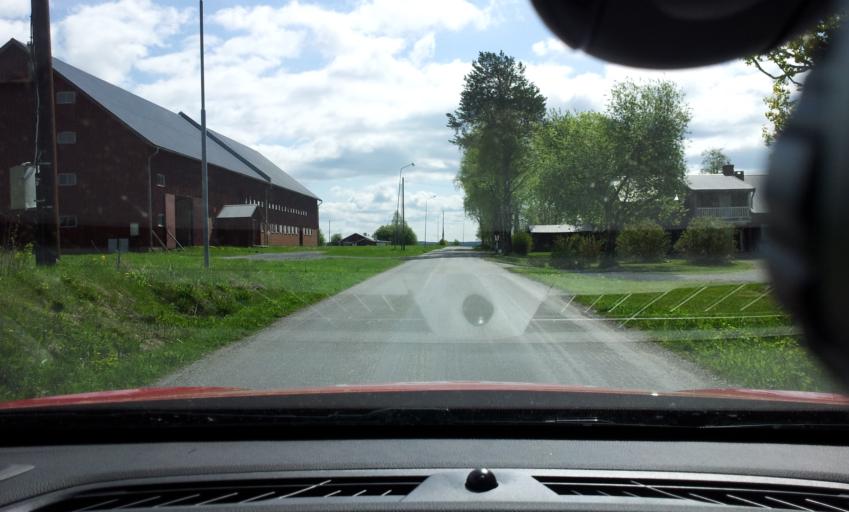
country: SE
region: Jaemtland
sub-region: OEstersunds Kommun
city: Ostersund
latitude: 63.0104
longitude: 14.6089
